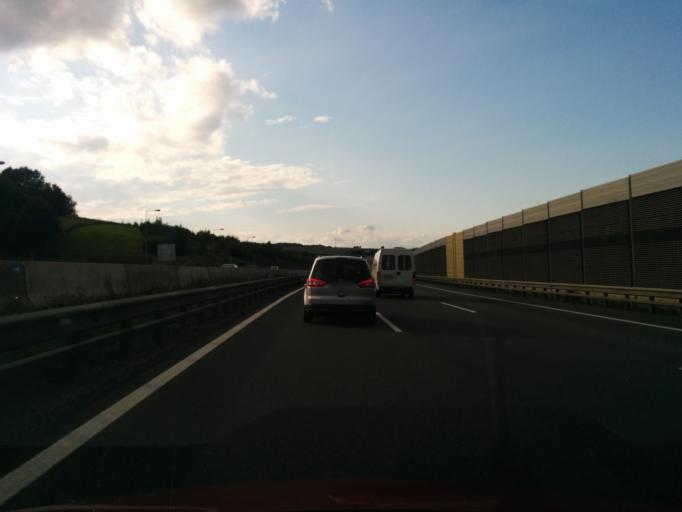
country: AT
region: Lower Austria
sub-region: Politischer Bezirk Sankt Polten
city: Altlengbach
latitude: 48.1570
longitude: 15.8918
